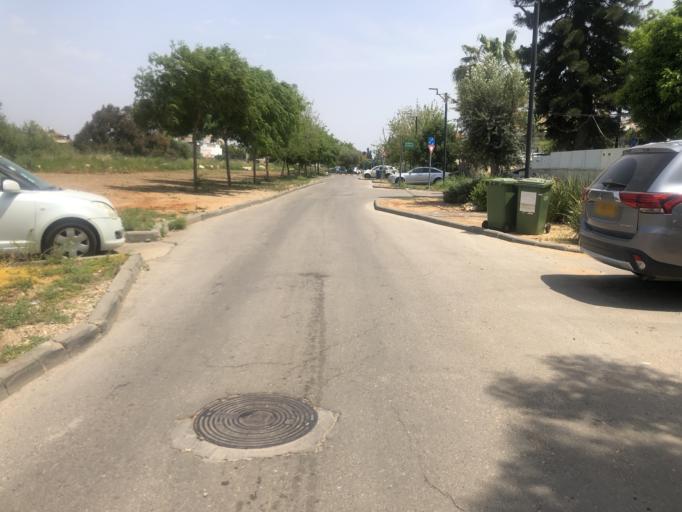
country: IL
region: Central District
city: Rosh Ha'Ayin
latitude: 32.0998
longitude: 34.9380
